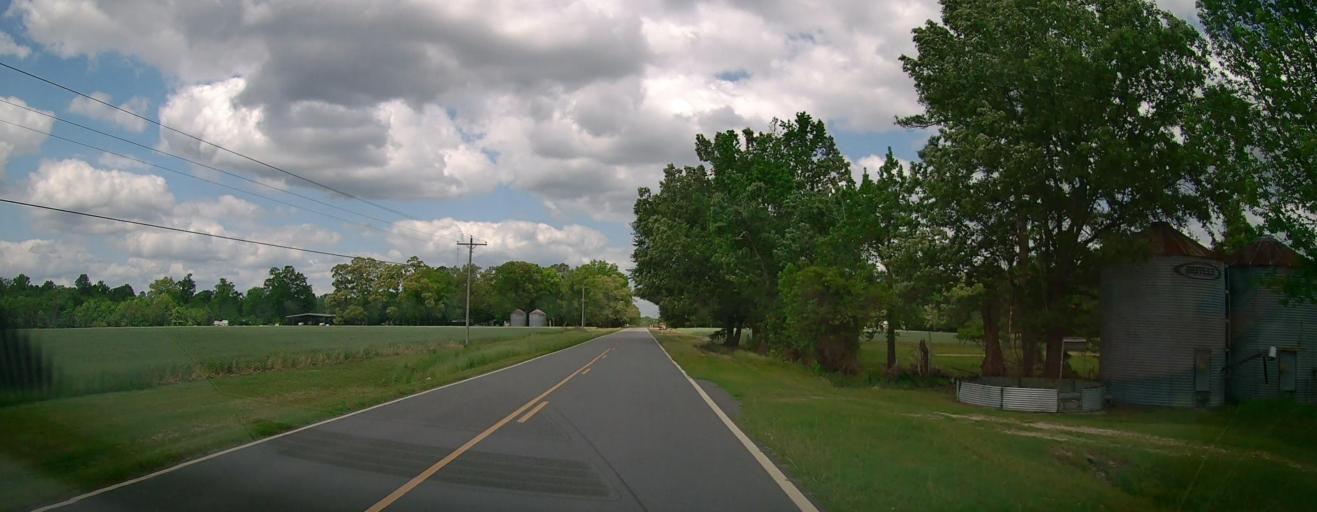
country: US
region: Georgia
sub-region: Laurens County
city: Dublin
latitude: 32.6089
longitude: -82.9640
